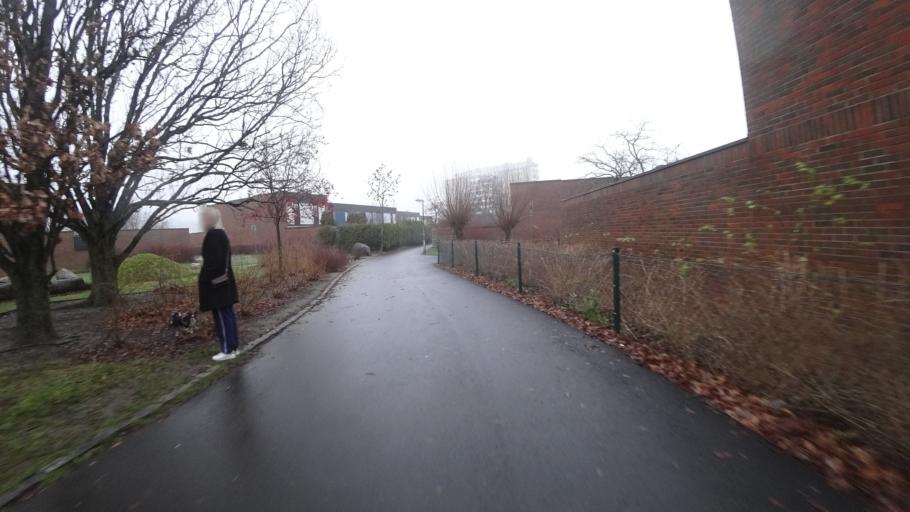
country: SE
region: Skane
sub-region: Malmo
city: Malmoe
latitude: 55.5755
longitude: 13.0012
